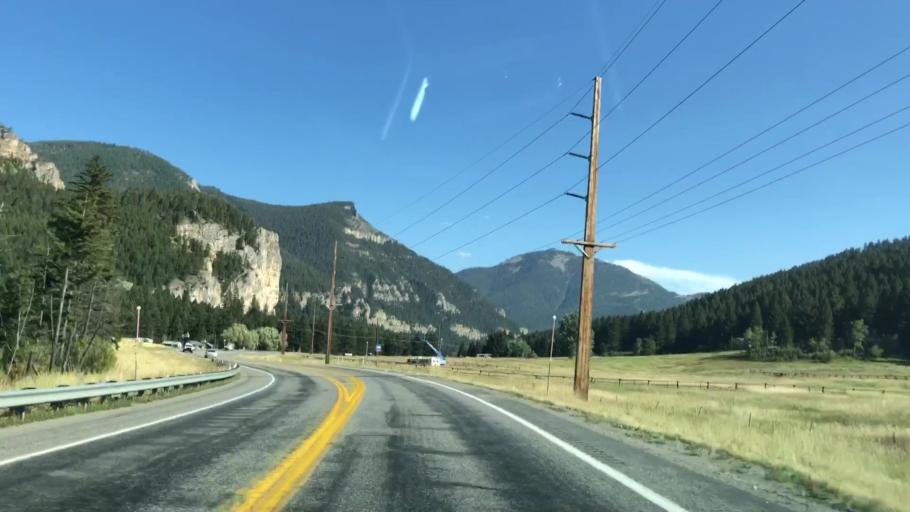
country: US
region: Montana
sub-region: Gallatin County
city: Four Corners
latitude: 45.4662
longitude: -111.2600
